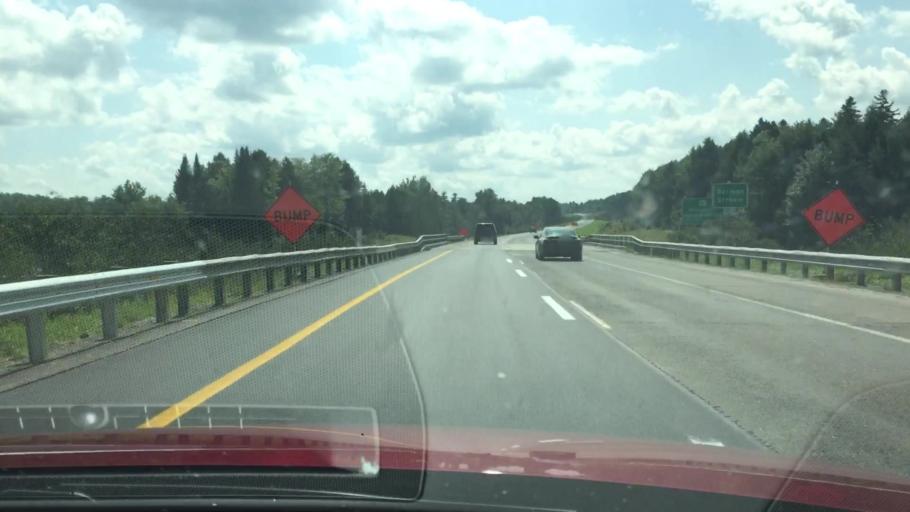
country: US
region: Maine
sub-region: Penobscot County
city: Medway
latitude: 45.6397
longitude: -68.5003
